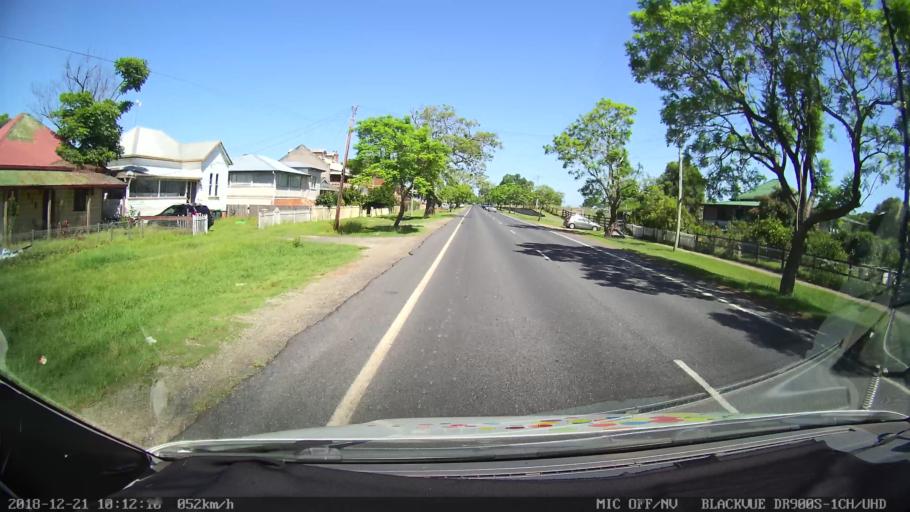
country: AU
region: New South Wales
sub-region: Clarence Valley
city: South Grafton
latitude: -29.7015
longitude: 152.9262
